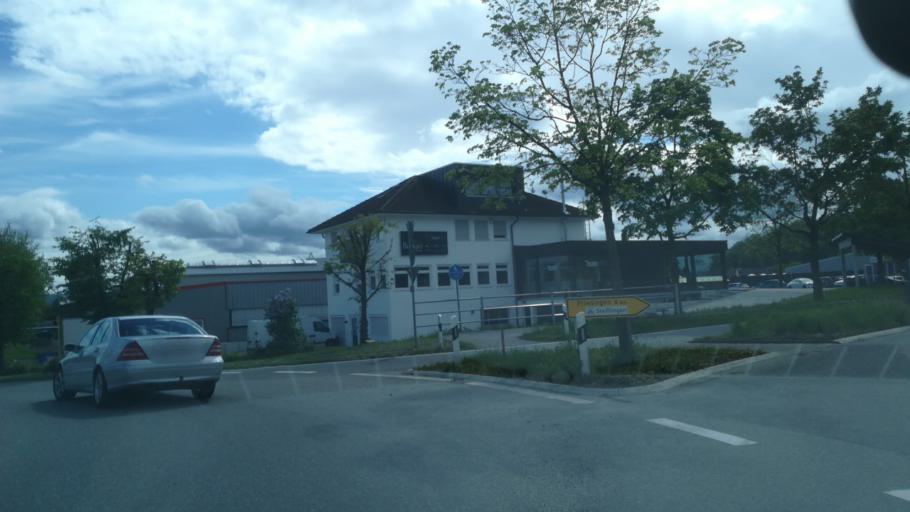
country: DE
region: Baden-Wuerttemberg
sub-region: Freiburg Region
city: Steisslingen
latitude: 47.7839
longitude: 8.9156
